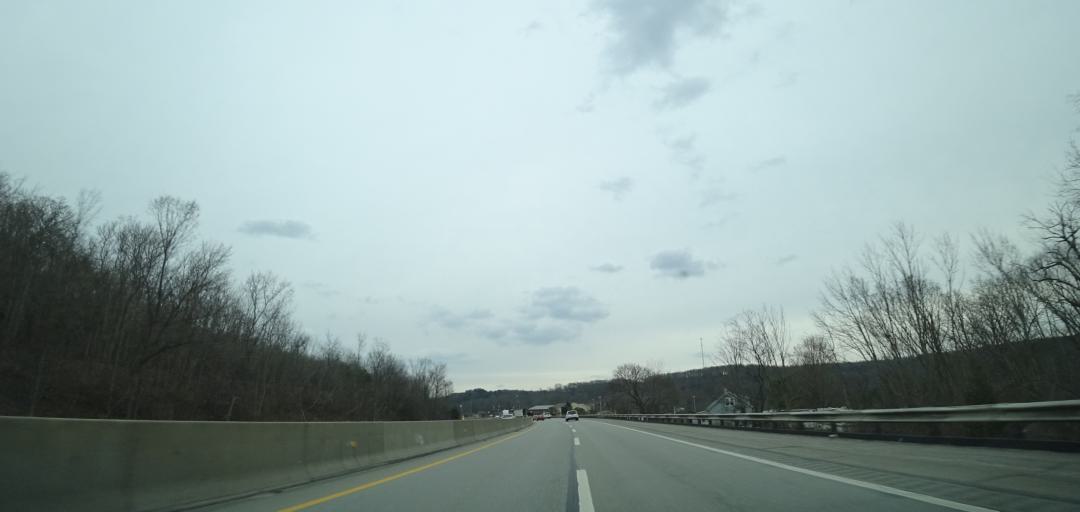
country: US
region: Pennsylvania
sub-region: Beaver County
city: Big Beaver
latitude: 40.8223
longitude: -80.3450
